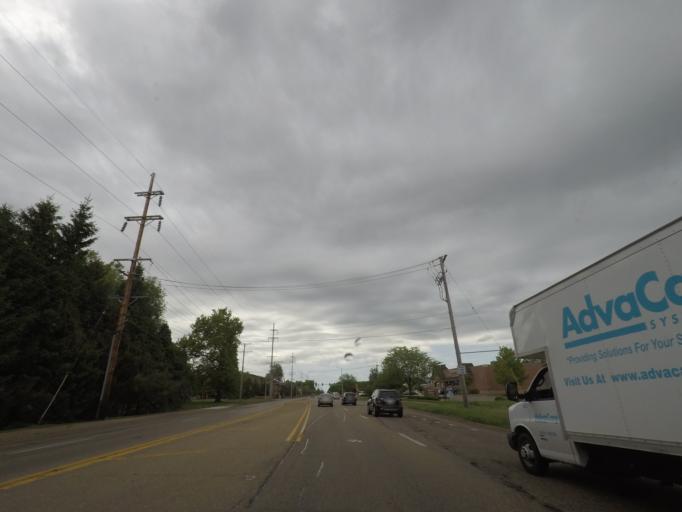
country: US
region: Illinois
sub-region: Winnebago County
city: Loves Park
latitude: 42.2793
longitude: -89.0290
